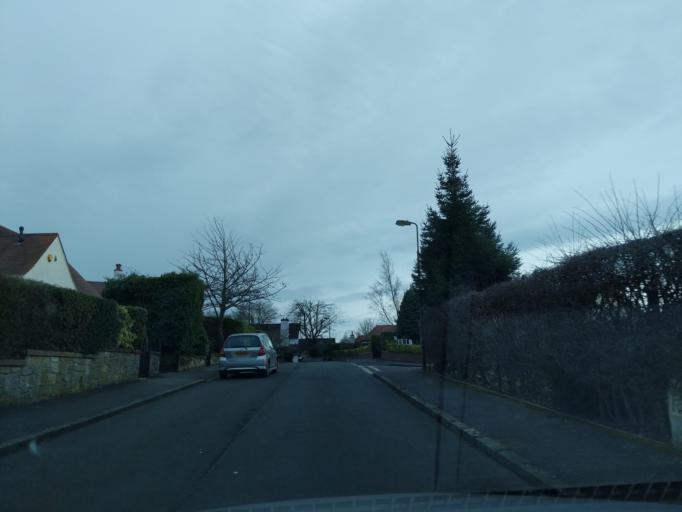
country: GB
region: Scotland
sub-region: Edinburgh
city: Currie
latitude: 55.9676
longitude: -3.3133
